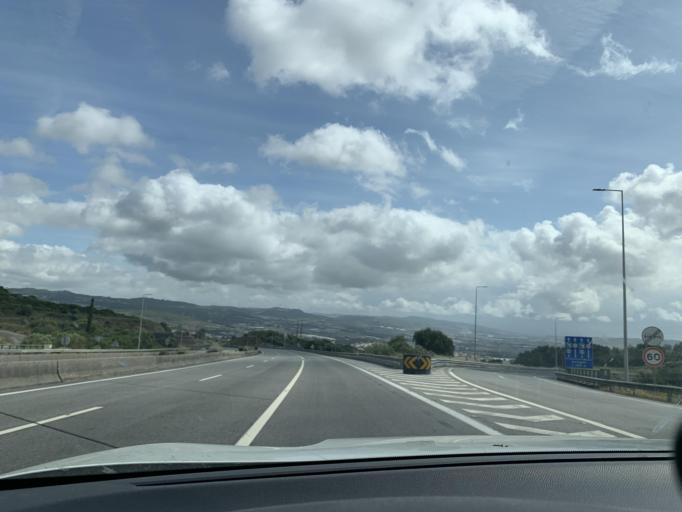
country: PT
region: Lisbon
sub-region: Odivelas
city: Ramada
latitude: 38.8225
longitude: -9.1939
